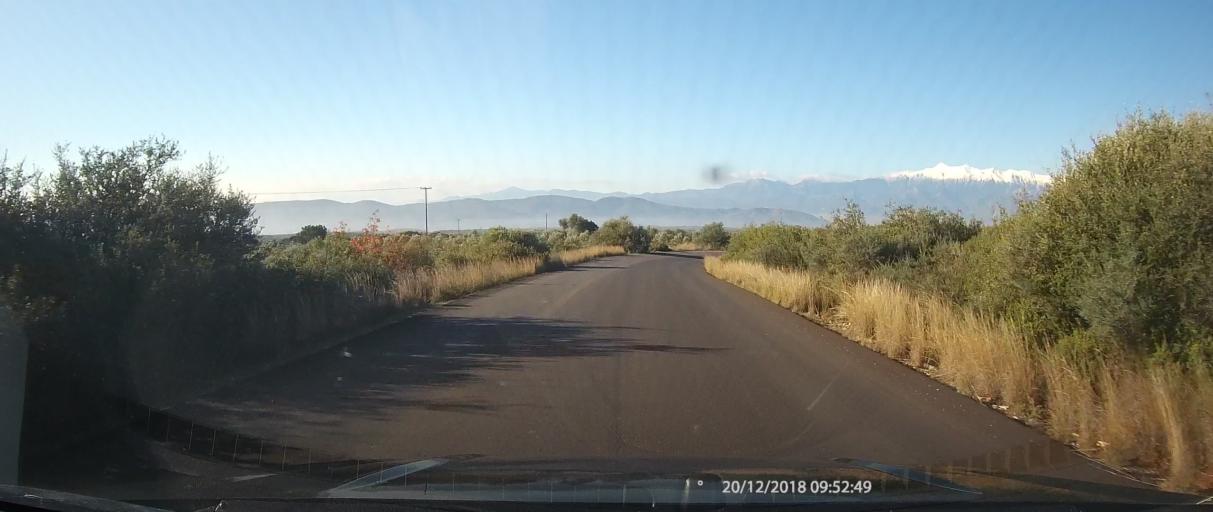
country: GR
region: Peloponnese
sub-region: Nomos Lakonias
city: Yerakion
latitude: 37.0080
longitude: 22.6391
